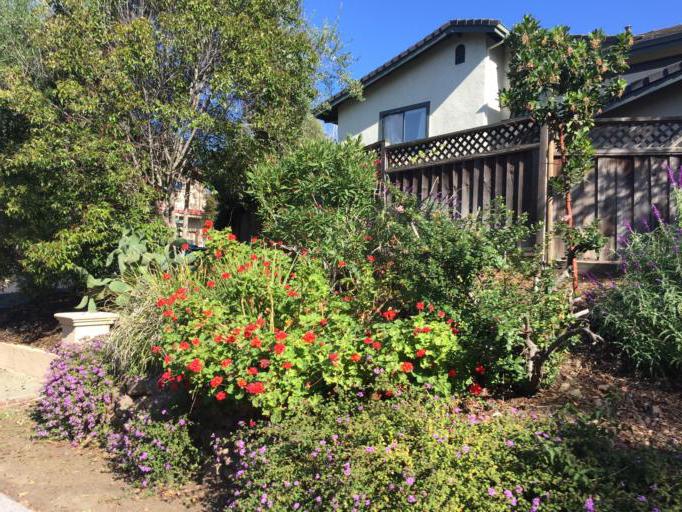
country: US
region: California
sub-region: San Mateo County
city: Emerald Lake Hills
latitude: 37.4712
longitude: -122.2553
